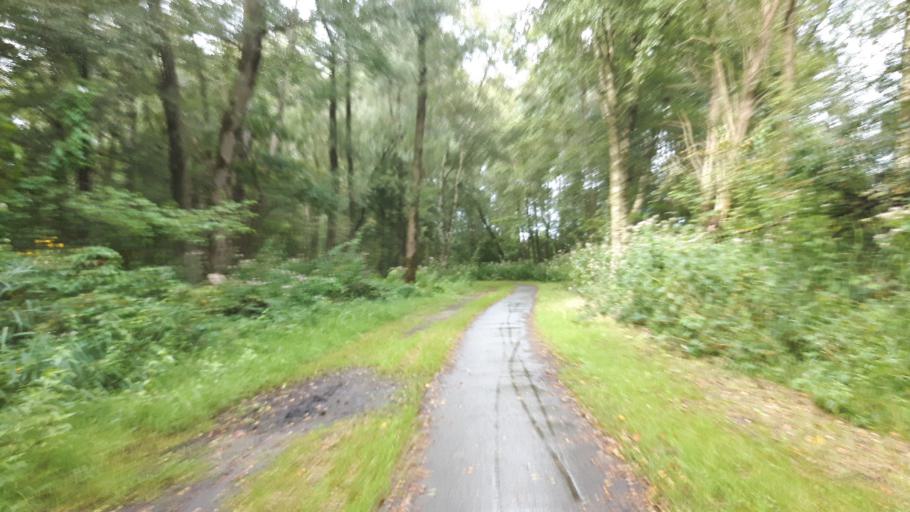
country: NL
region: Overijssel
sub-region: Gemeente Steenwijkerland
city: Blokzijl
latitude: 52.7637
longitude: 5.9591
